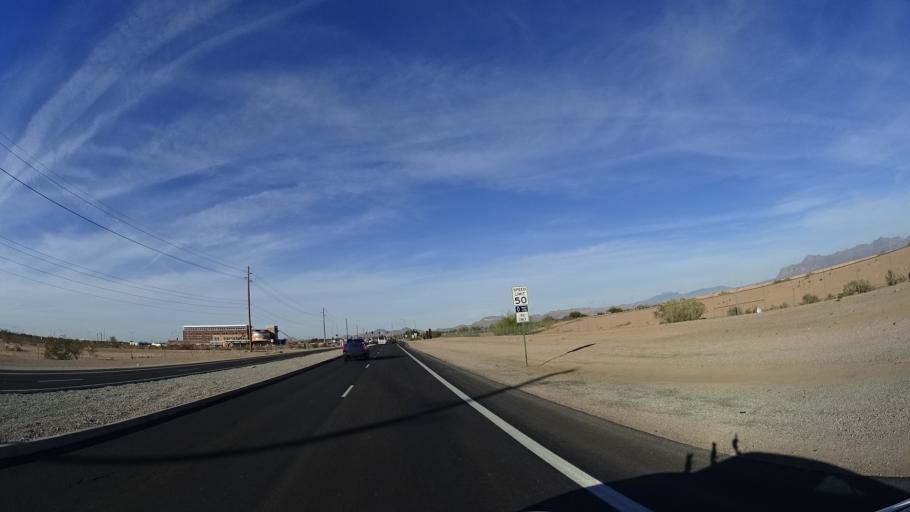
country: US
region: Arizona
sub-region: Maricopa County
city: Queen Creek
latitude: 33.3475
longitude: -111.6356
